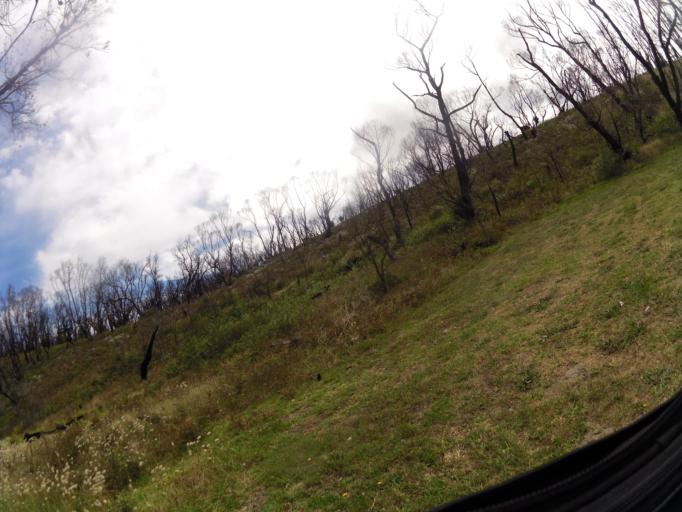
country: AU
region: Victoria
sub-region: East Gippsland
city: Lakes Entrance
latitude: -37.8029
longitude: 148.7410
